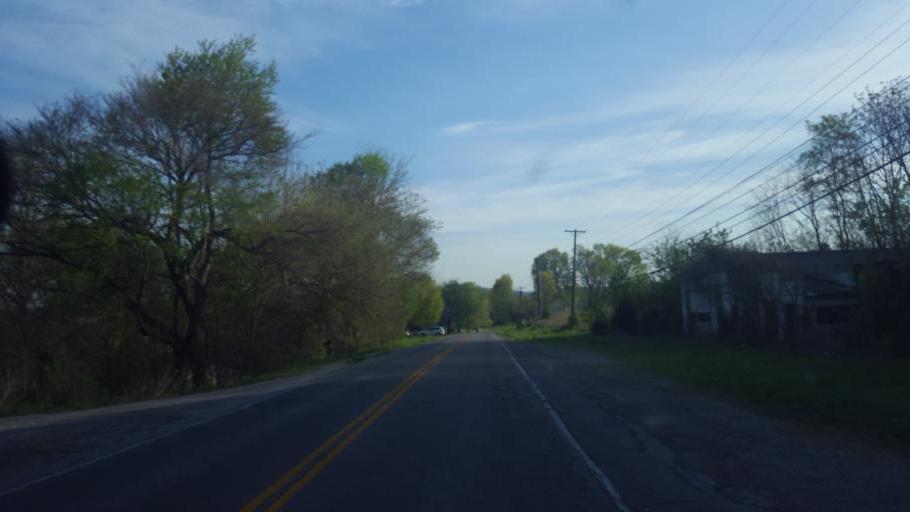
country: US
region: Kentucky
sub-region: Hart County
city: Munfordville
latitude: 37.2511
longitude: -85.8888
